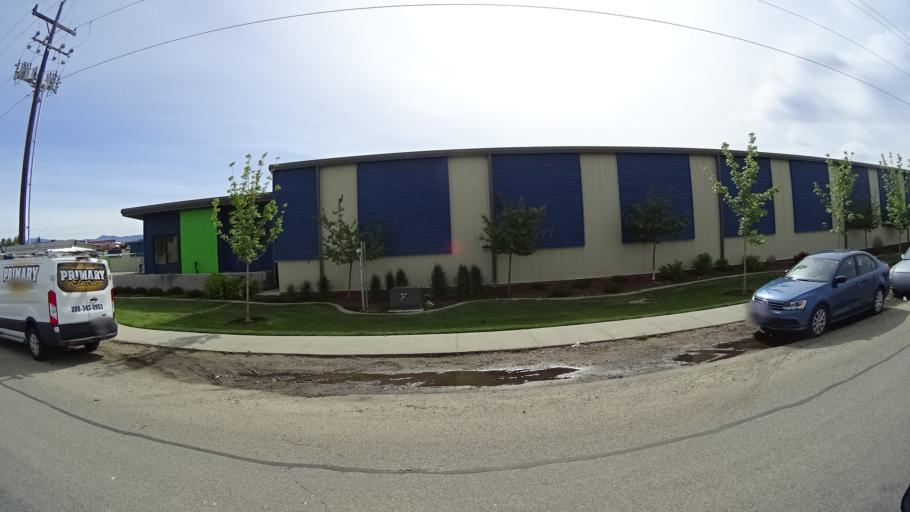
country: US
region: Idaho
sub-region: Ada County
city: Garden City
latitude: 43.5446
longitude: -116.2943
